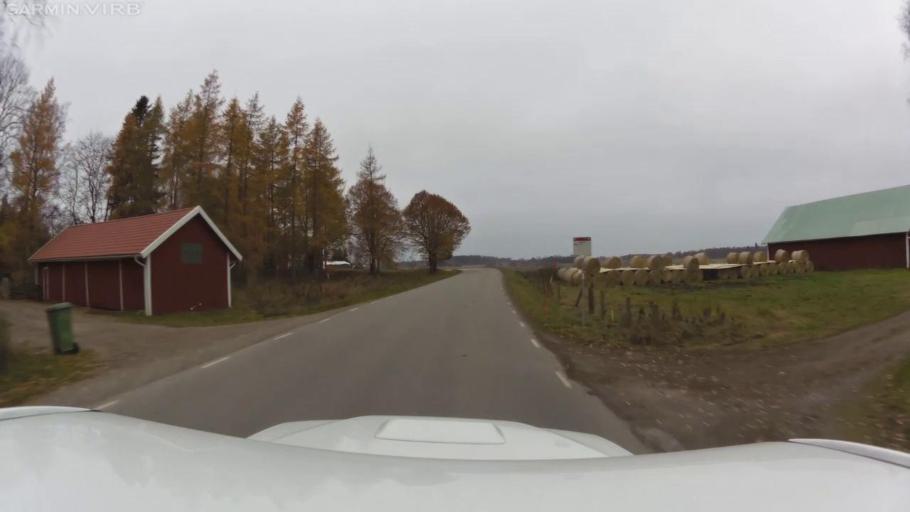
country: SE
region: OEstergoetland
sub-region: Linkopings Kommun
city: Vikingstad
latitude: 58.3650
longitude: 15.4208
